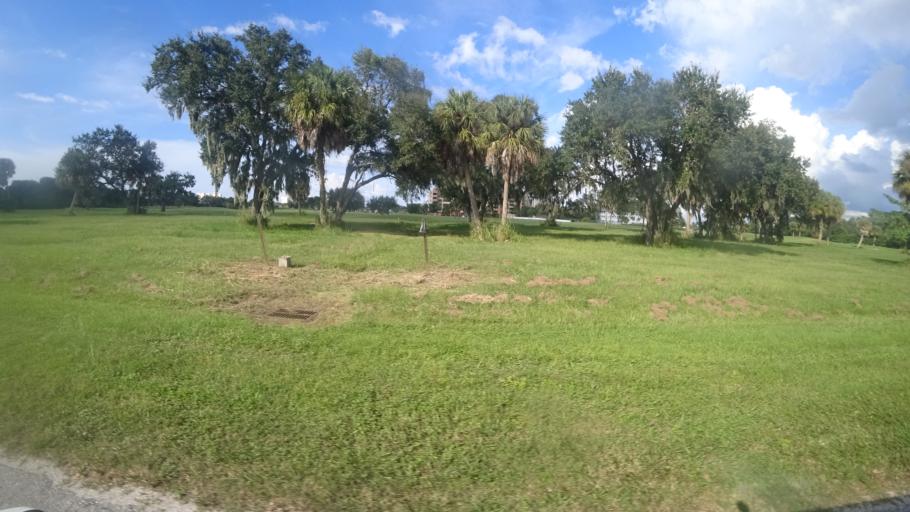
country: US
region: Florida
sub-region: Manatee County
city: Palmetto
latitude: 27.5323
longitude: -82.5827
